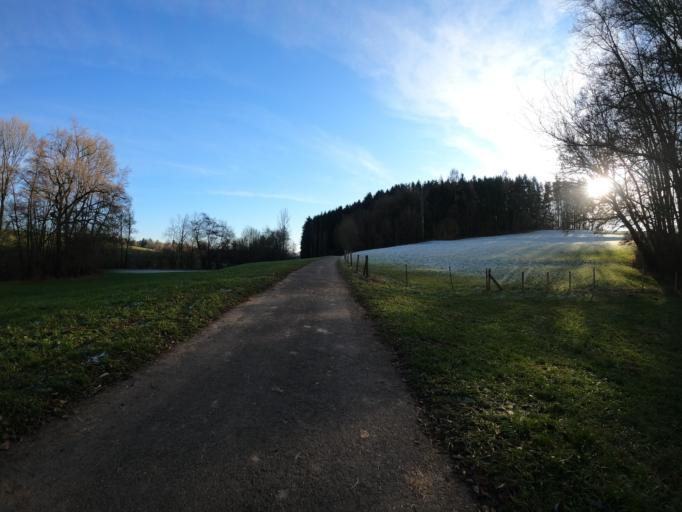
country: DE
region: Baden-Wuerttemberg
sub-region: Regierungsbezirk Stuttgart
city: Goeppingen
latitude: 48.6950
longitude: 9.6187
